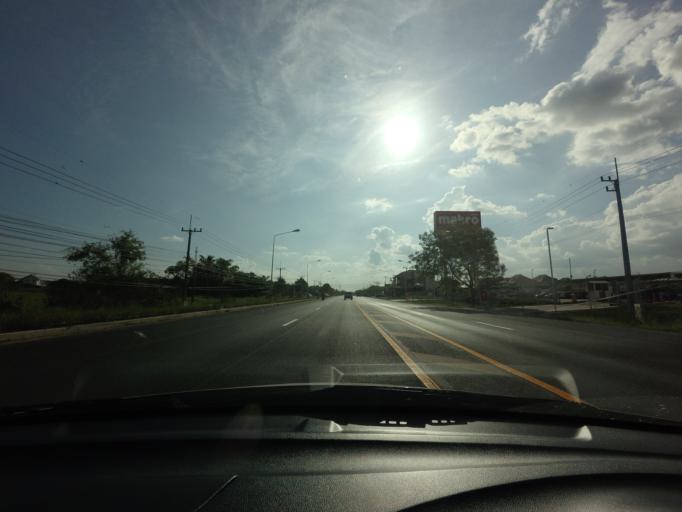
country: TH
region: Nakhon Nayok
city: Nakhon Nayok
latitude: 14.2263
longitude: 101.2348
